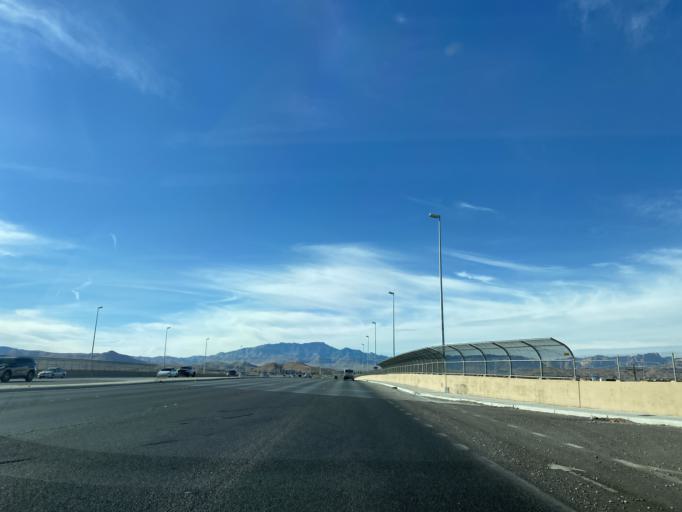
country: US
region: Nevada
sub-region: Clark County
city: Enterprise
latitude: 36.0257
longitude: -115.2258
